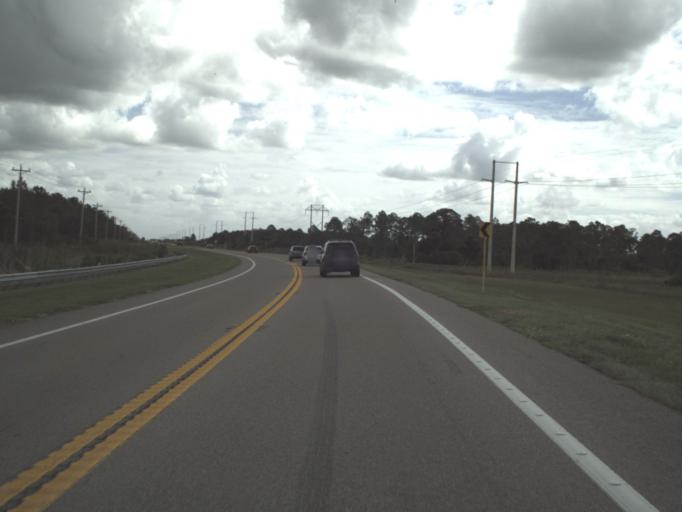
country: US
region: Florida
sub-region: Lee County
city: Lehigh Acres
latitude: 26.5355
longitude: -81.6302
